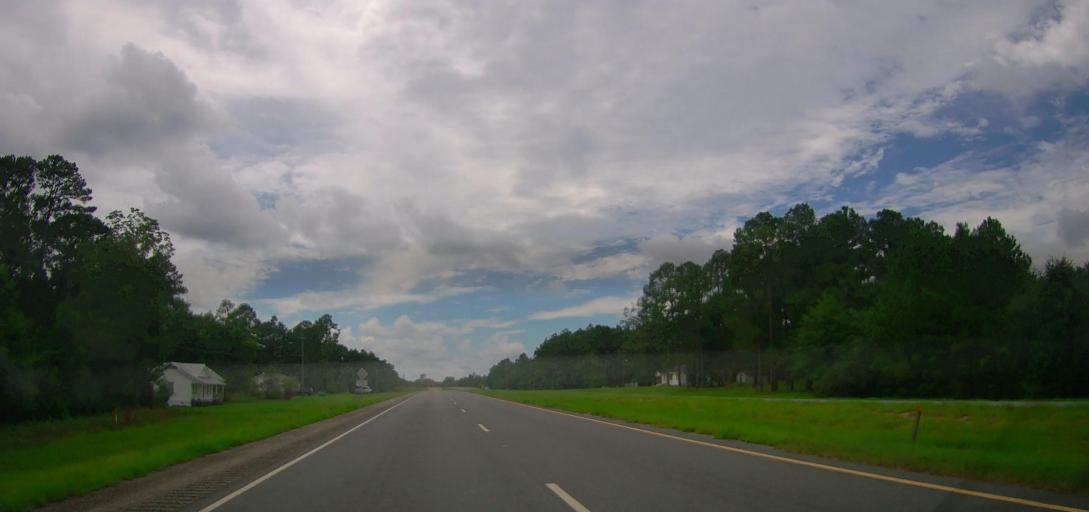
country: US
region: Georgia
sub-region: Telfair County
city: Helena
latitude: 32.1038
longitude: -83.0015
